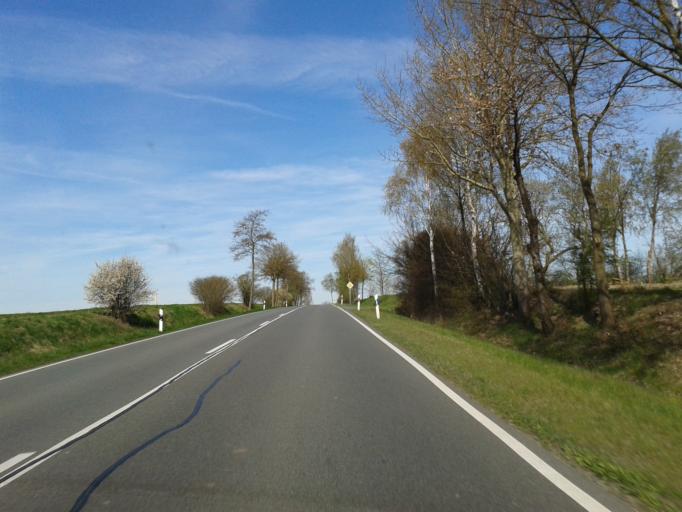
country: DE
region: Lower Saxony
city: Suhlendorf
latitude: 52.9439
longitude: 10.7352
